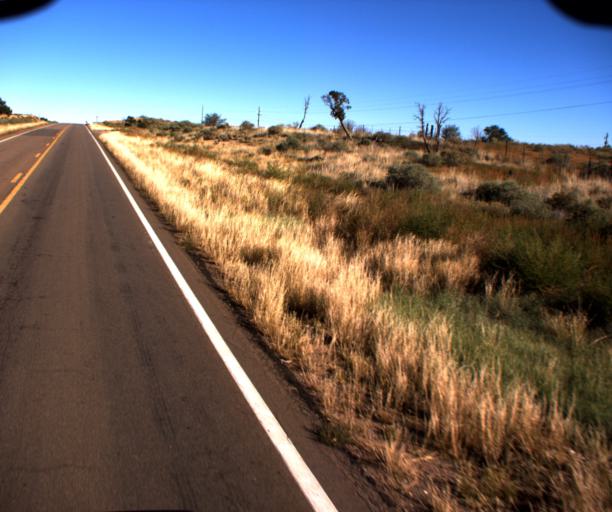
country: US
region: Arizona
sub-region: Navajo County
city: Snowflake
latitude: 34.5602
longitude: -110.0814
